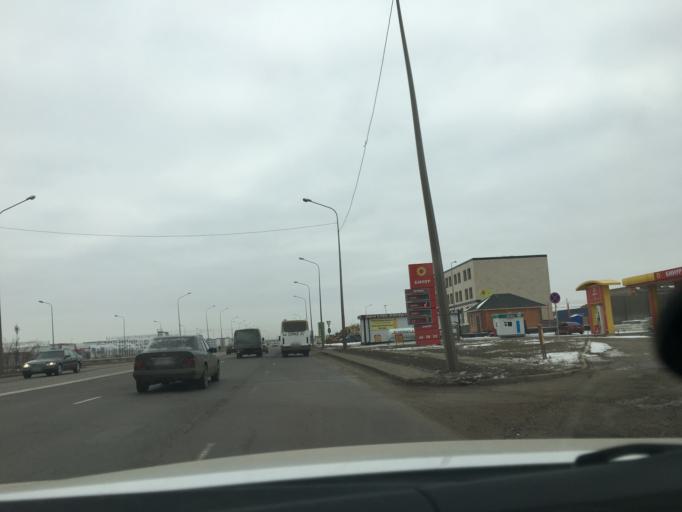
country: KZ
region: Astana Qalasy
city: Astana
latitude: 51.1595
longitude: 71.5208
